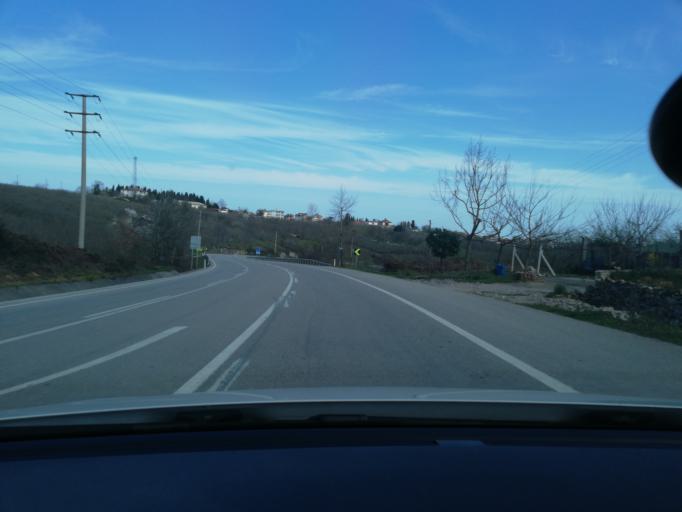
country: TR
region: Duzce
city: Akcakoca
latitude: 41.0749
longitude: 31.1126
